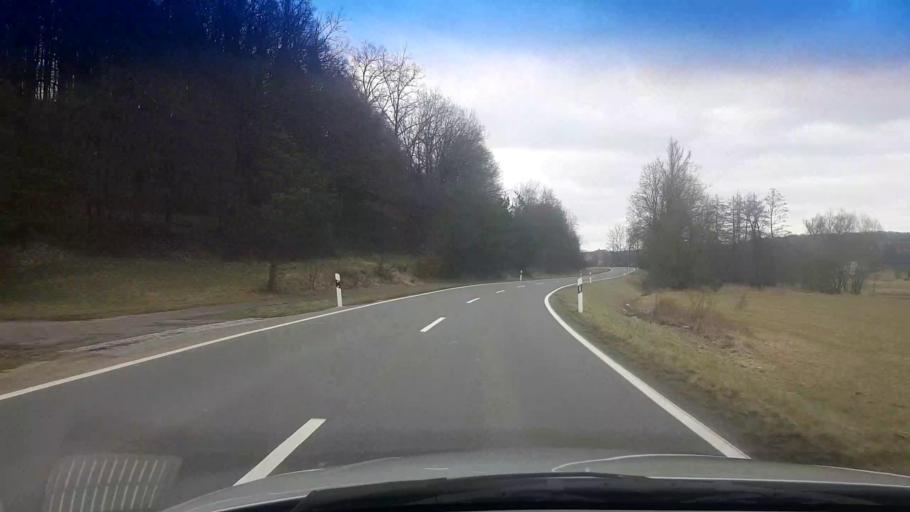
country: DE
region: Bavaria
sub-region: Upper Franconia
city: Priesendorf
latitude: 49.9223
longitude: 10.6734
